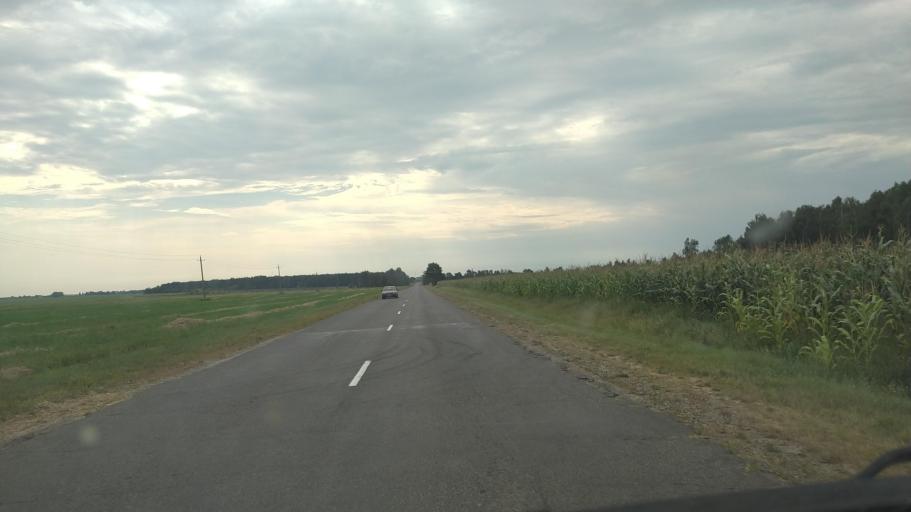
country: BY
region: Brest
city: Byaroza
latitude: 52.5659
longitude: 24.9001
